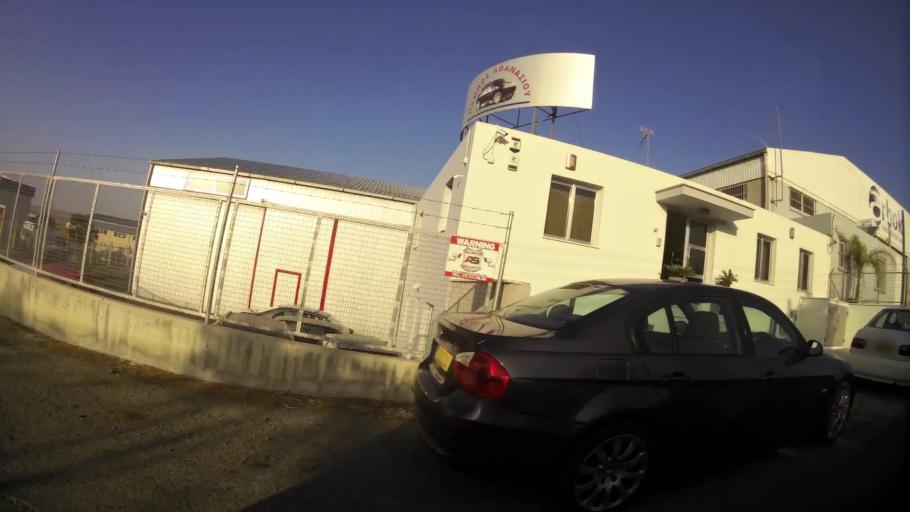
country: CY
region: Larnaka
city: Aradippou
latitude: 34.9316
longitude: 33.5843
